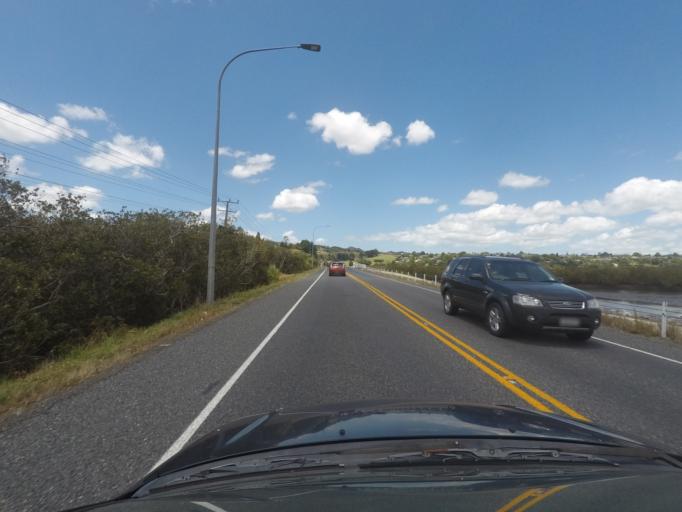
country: NZ
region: Northland
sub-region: Whangarei
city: Whangarei
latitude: -35.7371
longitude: 174.3545
